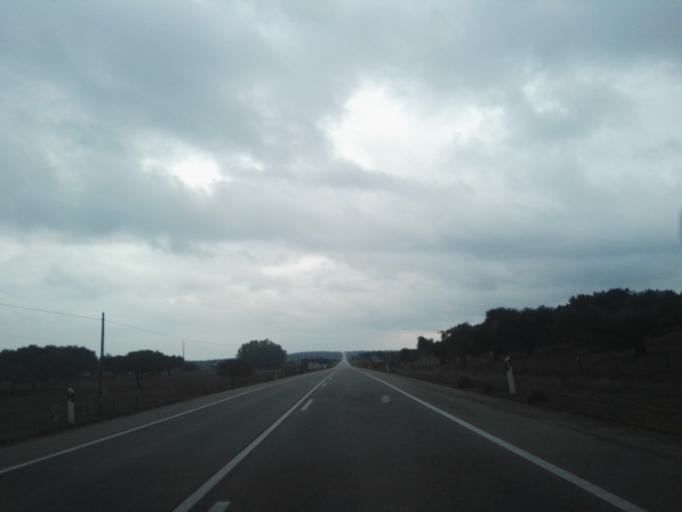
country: PT
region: Portalegre
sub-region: Portalegre
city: Alegrete
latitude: 39.1725
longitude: -7.3344
